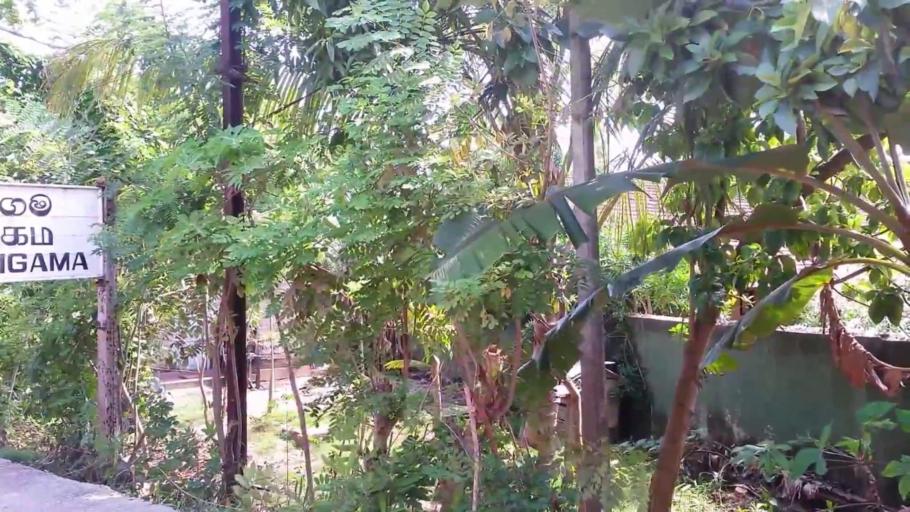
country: LK
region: Southern
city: Hikkaduwa
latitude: 6.1696
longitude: 80.0884
